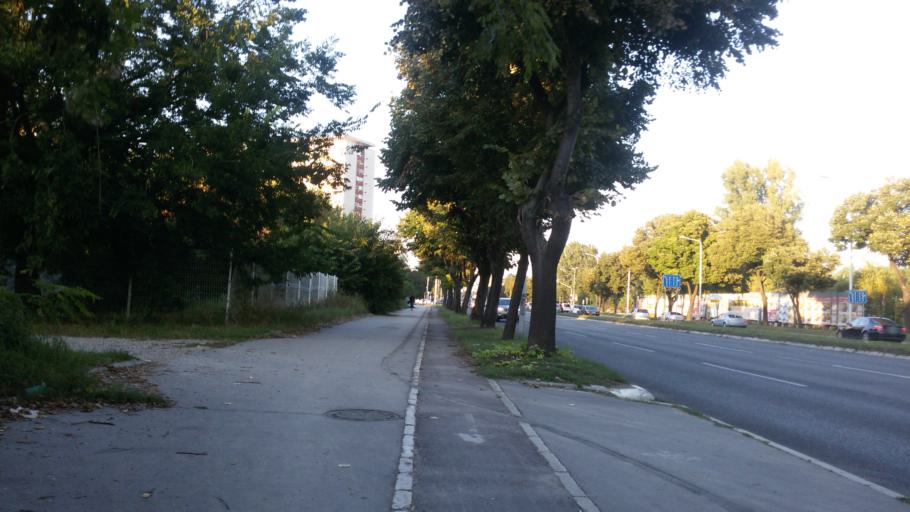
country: RS
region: Central Serbia
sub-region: Belgrade
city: Novi Beograd
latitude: 44.8137
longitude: 20.4034
